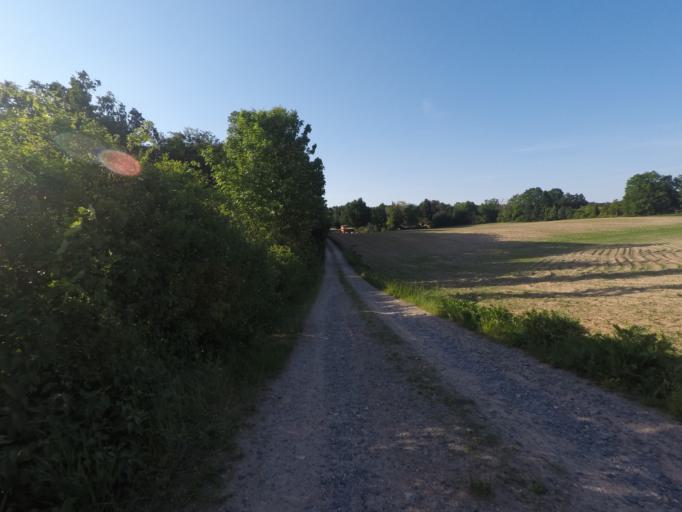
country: DE
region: Brandenburg
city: Joachimsthal
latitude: 52.9032
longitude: 13.7021
